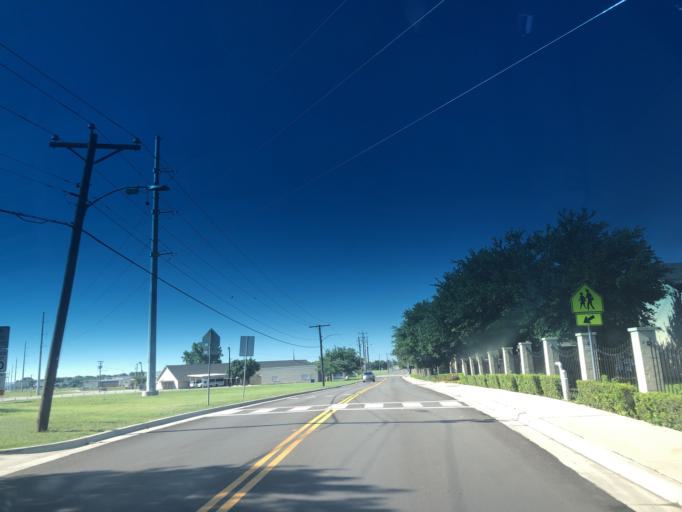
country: US
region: Texas
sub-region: Dallas County
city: Grand Prairie
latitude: 32.7158
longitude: -97.0197
